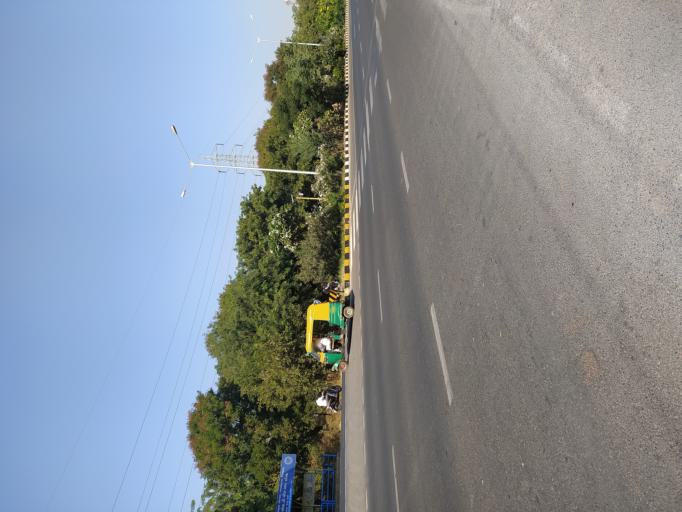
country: IN
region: Gujarat
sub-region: Gandhinagar
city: Adalaj
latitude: 23.1471
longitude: 72.6345
